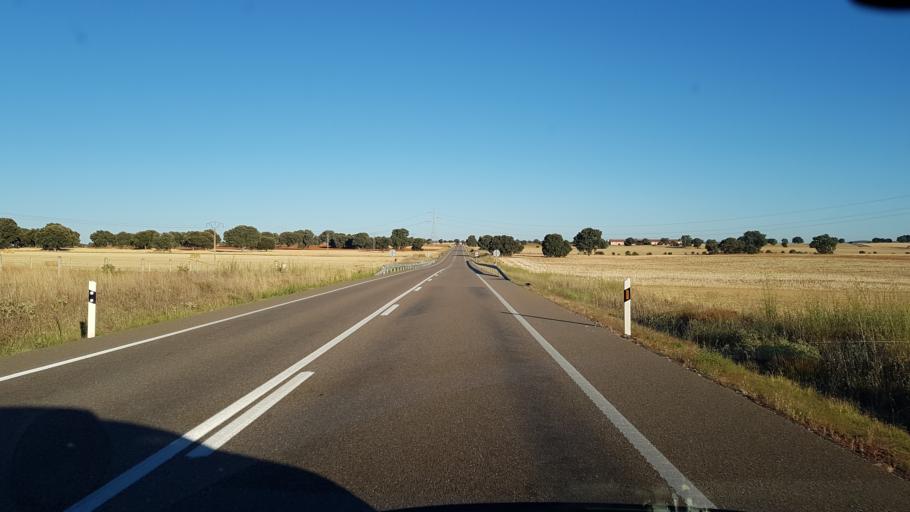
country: ES
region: Castille and Leon
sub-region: Provincia de Zamora
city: Palacios del Pan
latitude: 41.5437
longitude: -5.8728
